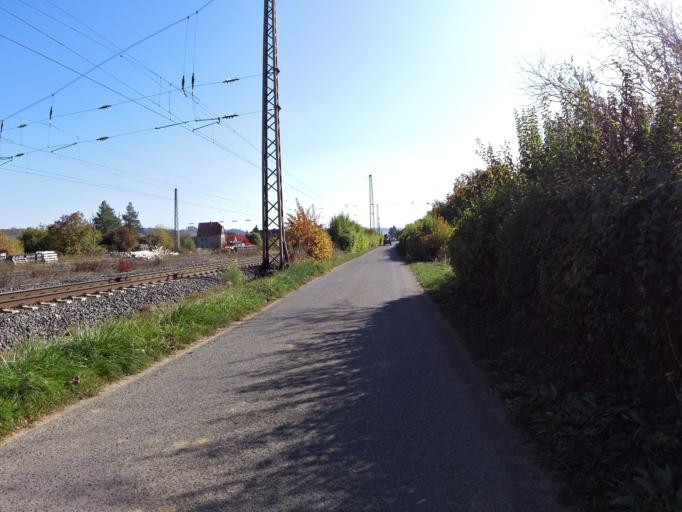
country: DE
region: Bavaria
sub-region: Regierungsbezirk Unterfranken
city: Winterhausen
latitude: 49.7111
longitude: 10.0081
